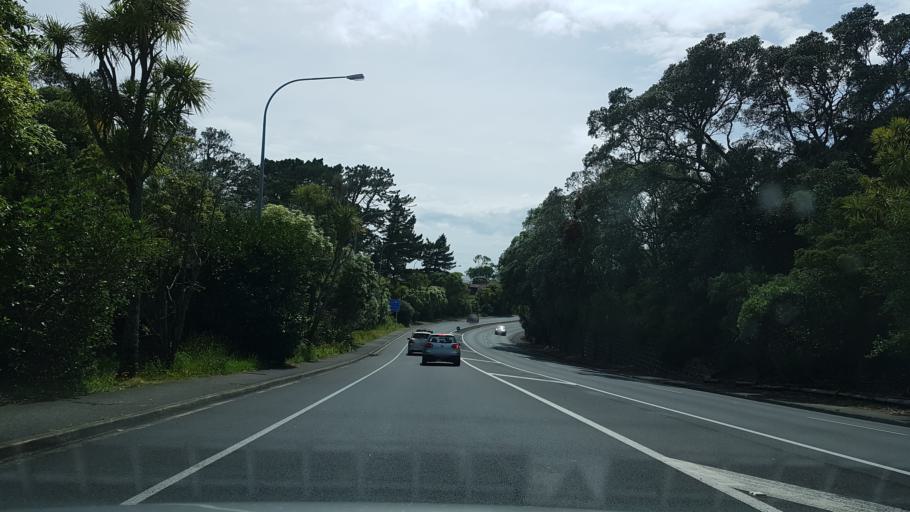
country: NZ
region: Auckland
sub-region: Auckland
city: North Shore
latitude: -36.8106
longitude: 174.7218
